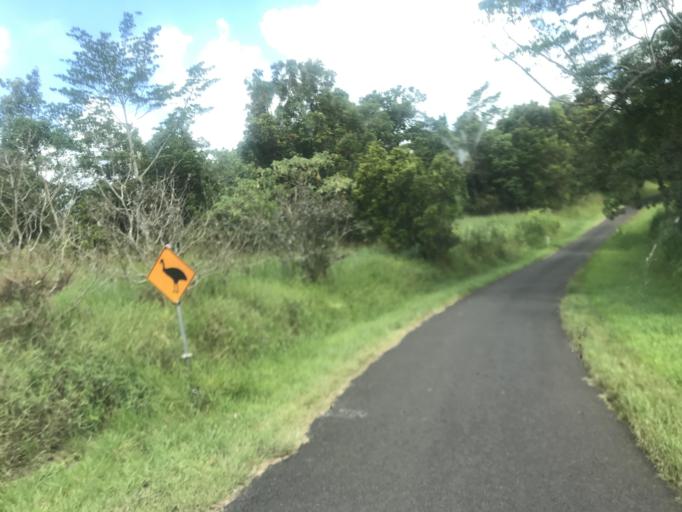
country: AU
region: Queensland
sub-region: Tablelands
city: Ravenshoe
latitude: -17.5413
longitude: 145.6910
